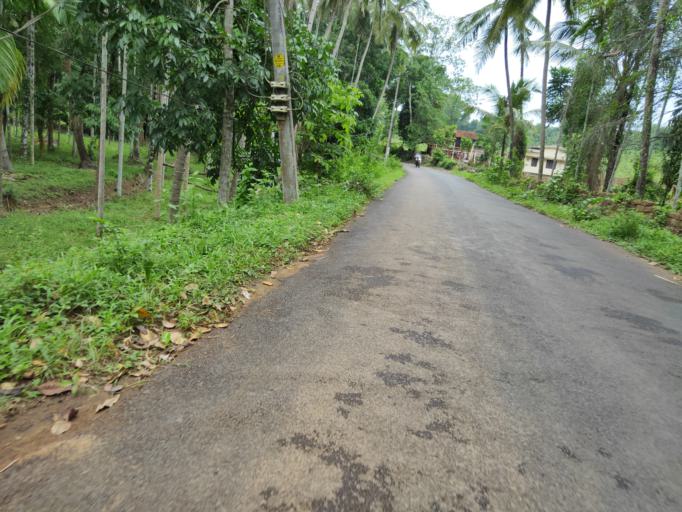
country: IN
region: Kerala
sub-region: Malappuram
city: Manjeri
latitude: 11.2364
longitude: 76.2472
